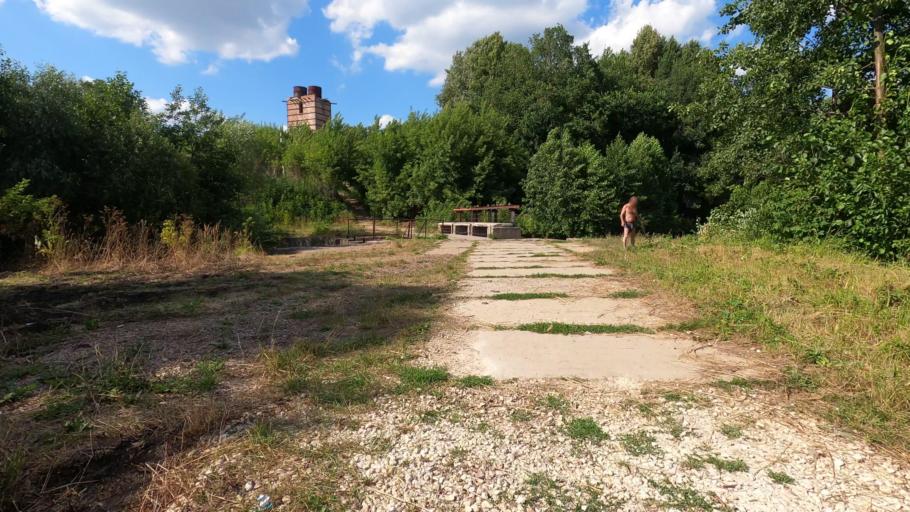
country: RU
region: Moskovskaya
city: Peski
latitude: 55.2185
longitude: 38.7570
